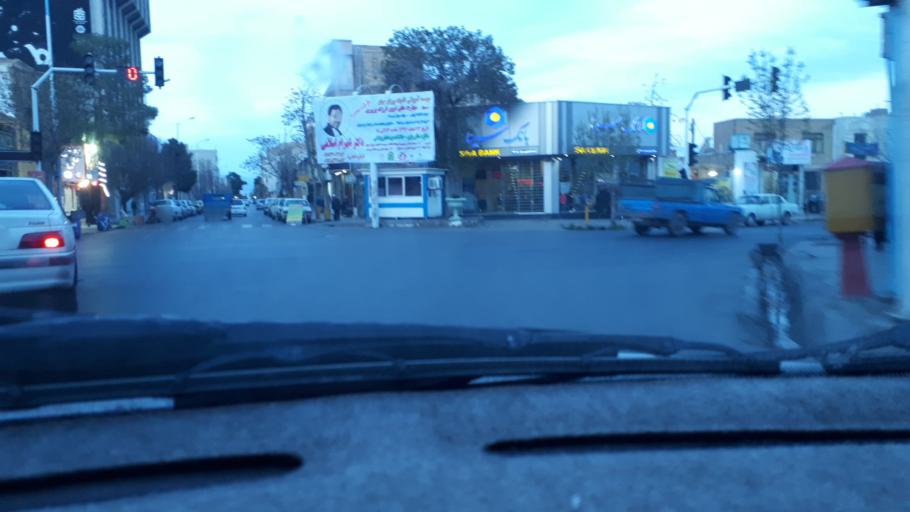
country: IR
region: Semnan
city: Semnan
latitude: 35.5674
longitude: 53.4014
